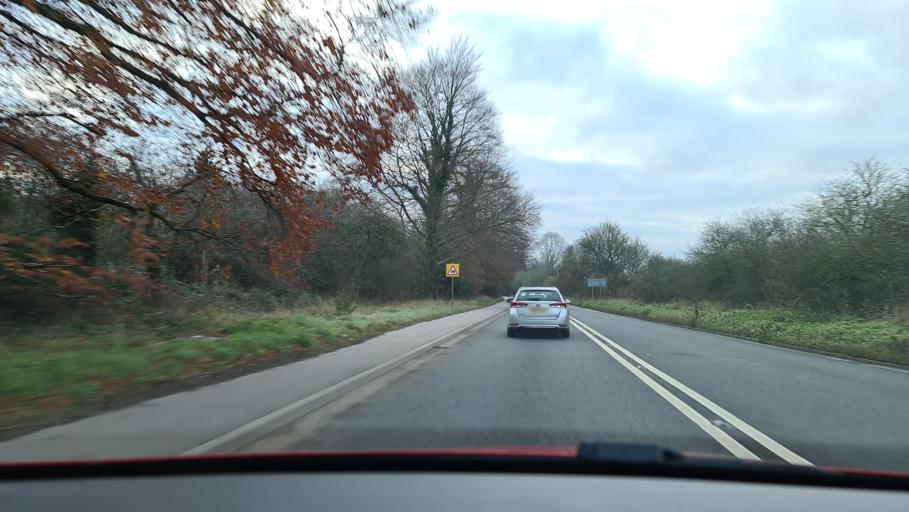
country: GB
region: England
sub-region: Buckinghamshire
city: Princes Risborough
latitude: 51.6647
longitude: -0.8097
